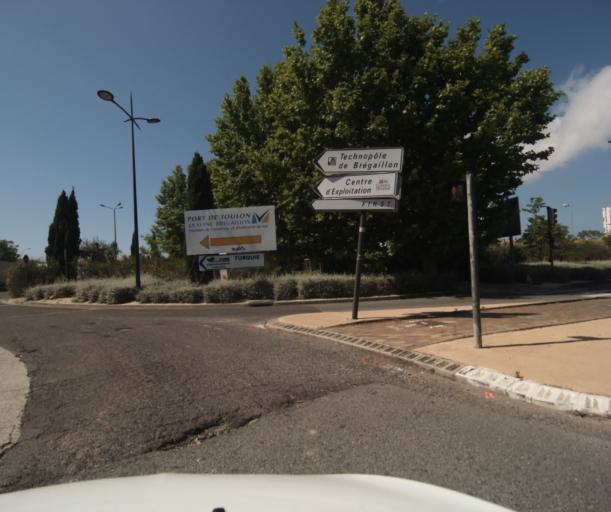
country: FR
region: Provence-Alpes-Cote d'Azur
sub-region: Departement du Var
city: La Seyne-sur-Mer
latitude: 43.1112
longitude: 5.8808
